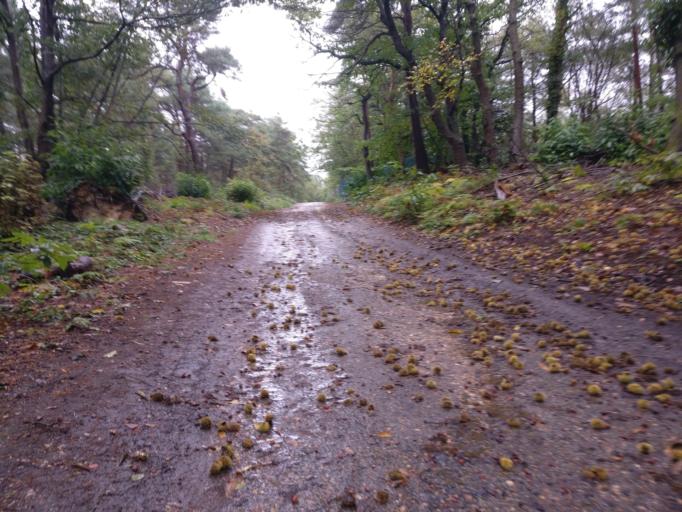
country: GB
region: England
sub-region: Surrey
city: Frimley
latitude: 51.3146
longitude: -0.7039
